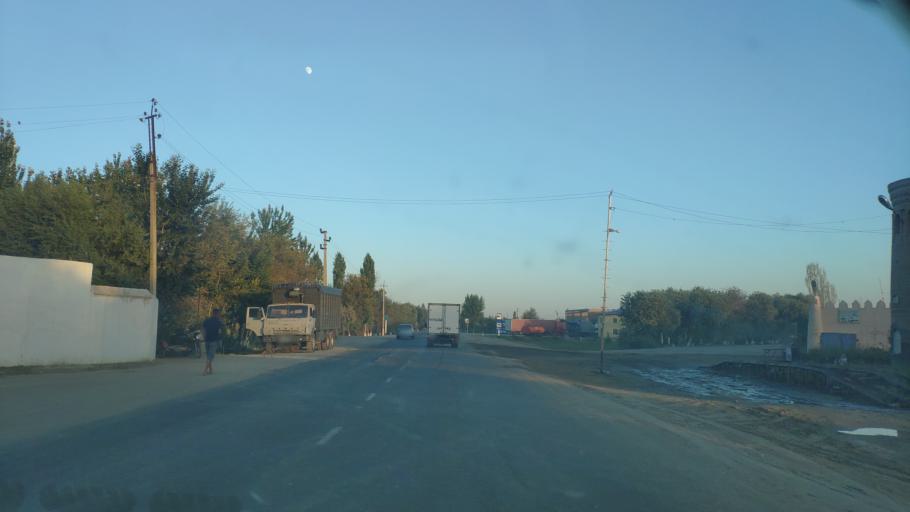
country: UZ
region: Karakalpakstan
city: To'rtko'l Shahri
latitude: 41.5672
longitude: 60.9518
